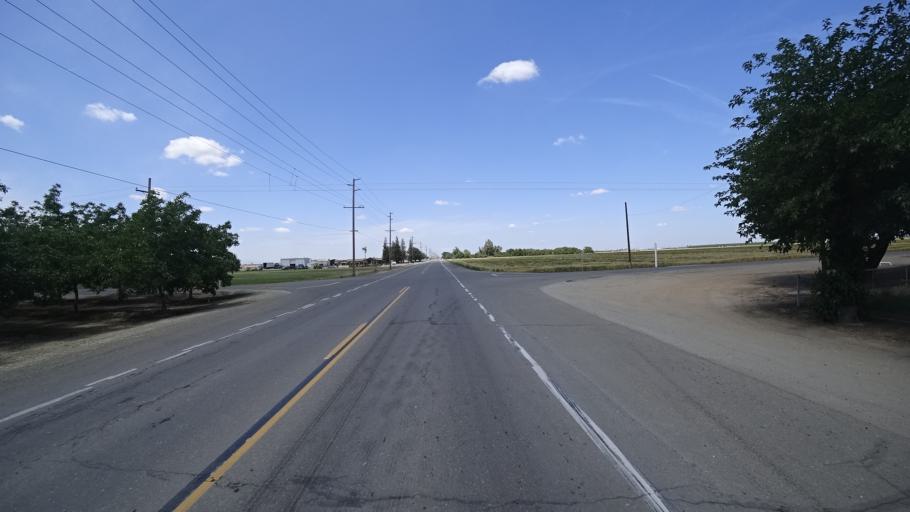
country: US
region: California
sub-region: Kings County
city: Home Garden
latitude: 36.2986
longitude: -119.5647
